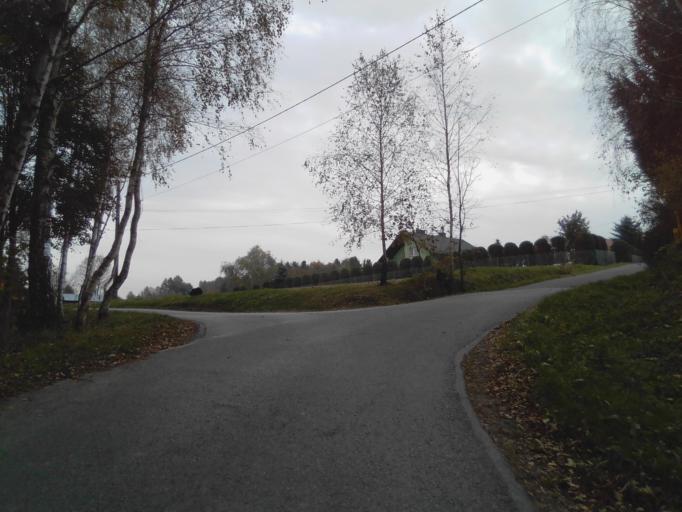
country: PL
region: Subcarpathian Voivodeship
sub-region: Powiat strzyzowski
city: Gwoznica Gorna
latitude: 49.8401
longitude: 21.9779
